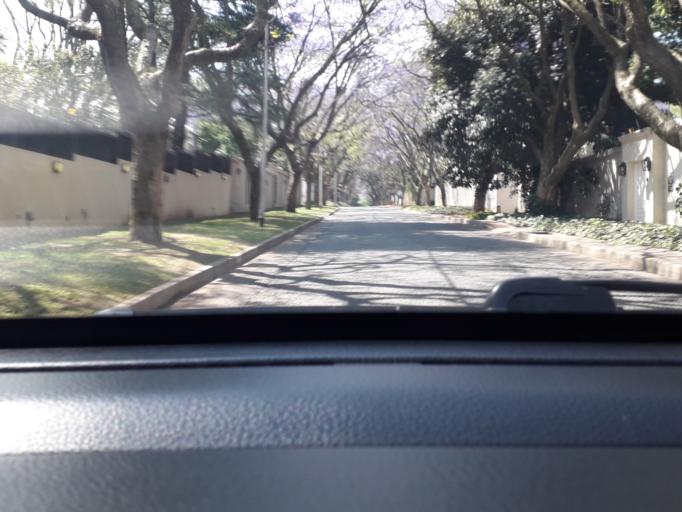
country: ZA
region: Gauteng
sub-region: City of Johannesburg Metropolitan Municipality
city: Johannesburg
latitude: -26.1391
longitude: 28.0500
